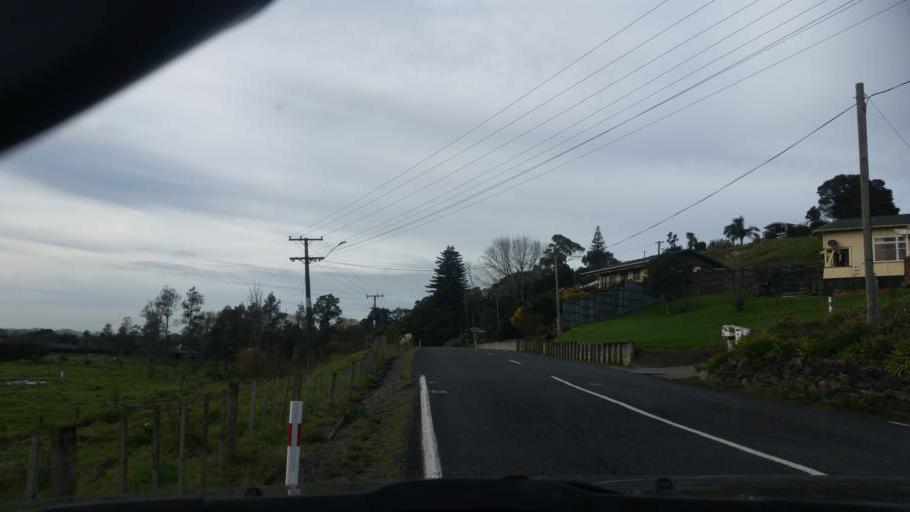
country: NZ
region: Northland
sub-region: Kaipara District
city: Dargaville
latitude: -35.9523
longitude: 173.8564
